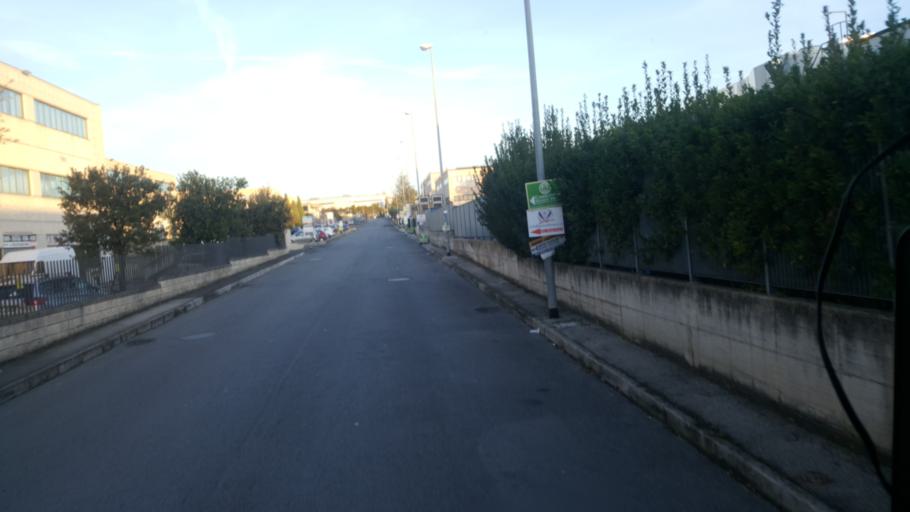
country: IT
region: Latium
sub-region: Citta metropolitana di Roma Capitale
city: Formello
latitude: 42.0497
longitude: 12.4009
